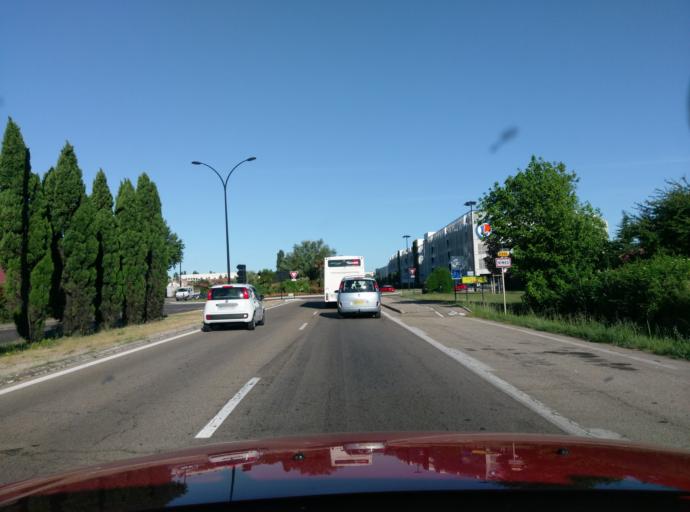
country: FR
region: Languedoc-Roussillon
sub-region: Departement du Gard
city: Rodilhan
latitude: 43.8364
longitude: 4.3955
